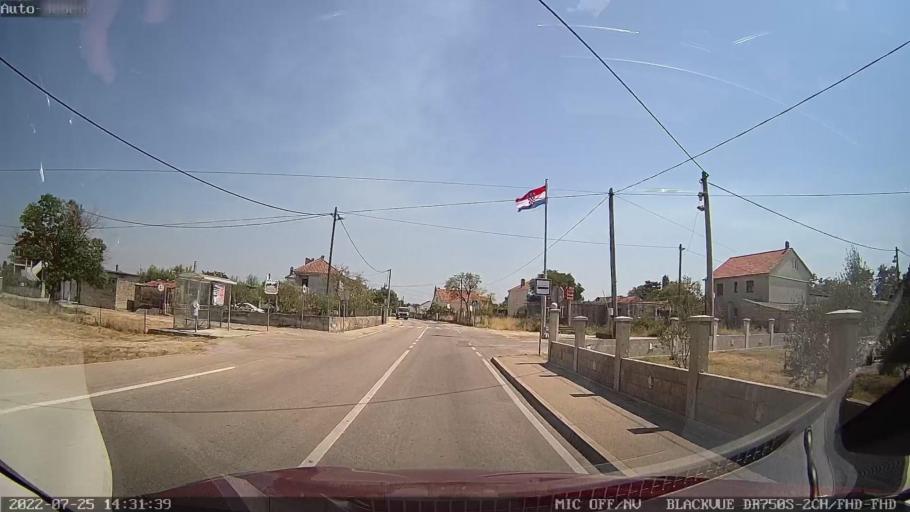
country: HR
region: Zadarska
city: Galovac
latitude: 44.1096
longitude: 15.3740
